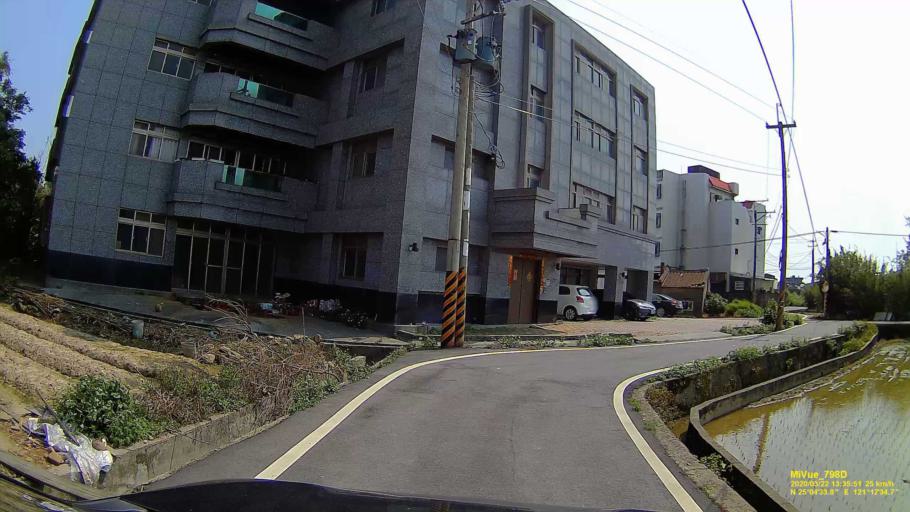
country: TW
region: Taiwan
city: Taoyuan City
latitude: 25.0760
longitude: 121.2096
